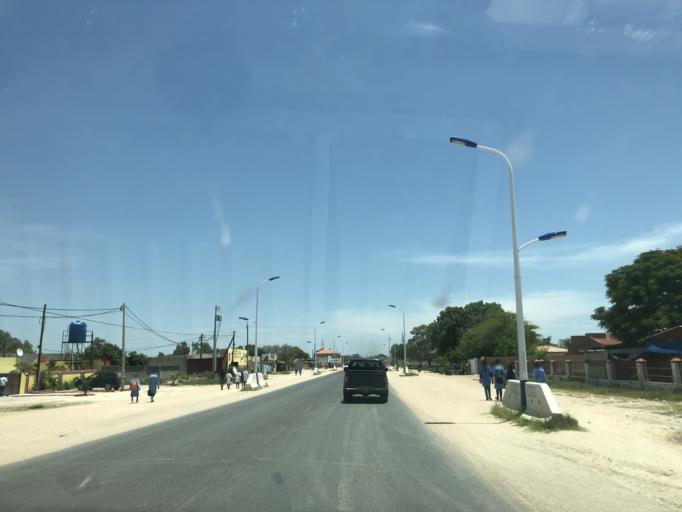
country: AO
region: Cunene
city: Ondjiva
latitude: -17.0795
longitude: 15.7371
